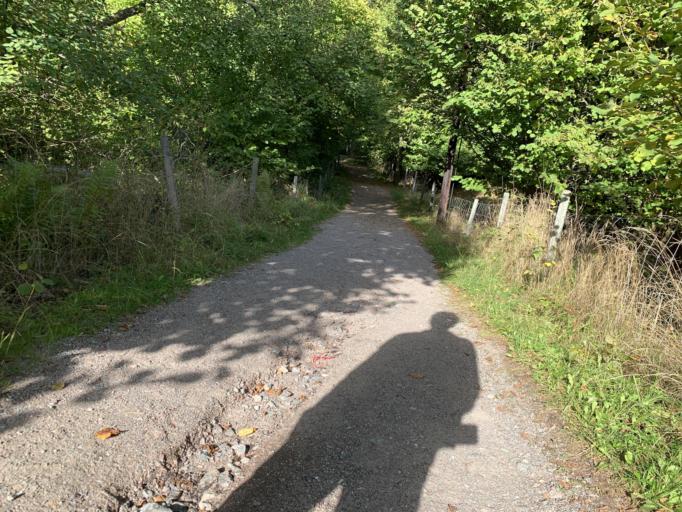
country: SE
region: Vaestmanland
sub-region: Vasteras
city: Vasteras
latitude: 59.5627
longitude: 16.6239
